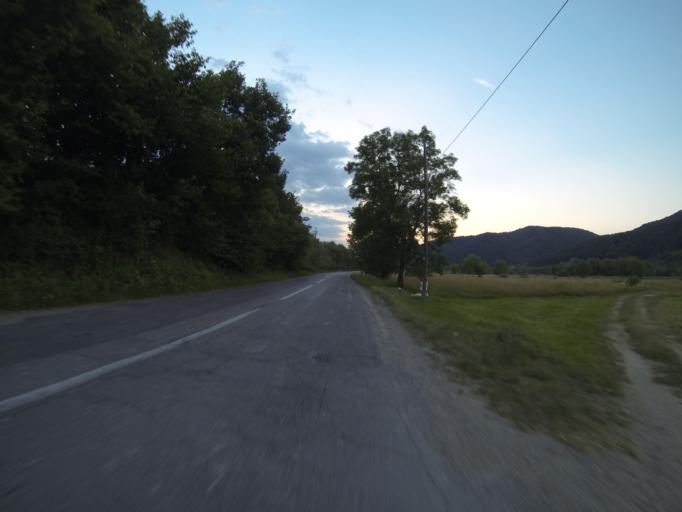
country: RO
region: Brasov
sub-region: Comuna Sinca Noua
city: Sinca Noua
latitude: 45.7300
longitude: 25.2349
